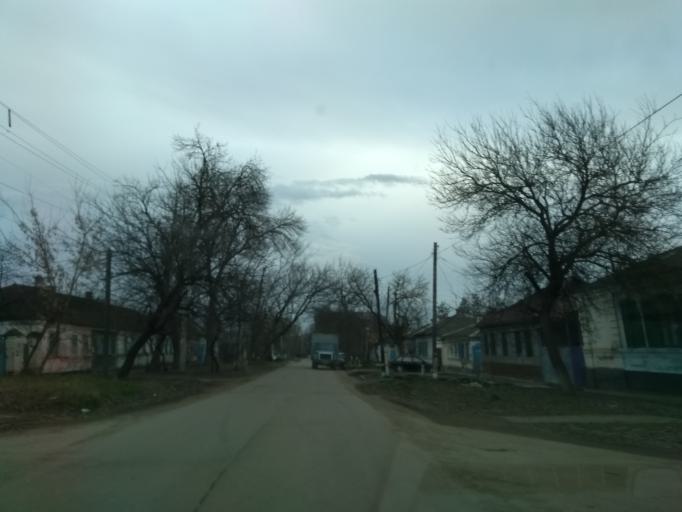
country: RU
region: Stavropol'skiy
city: Georgiyevsk
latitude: 44.1498
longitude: 43.4670
